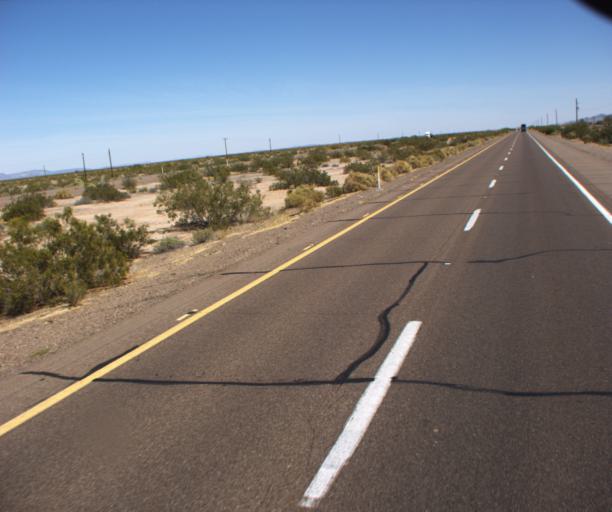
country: US
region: Arizona
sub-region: Yuma County
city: Wellton
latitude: 32.7403
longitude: -113.6884
